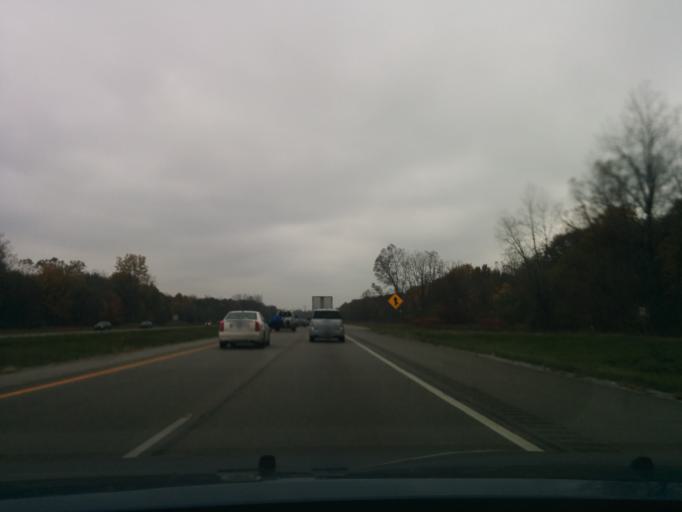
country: US
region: Michigan
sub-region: Wayne County
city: Plymouth
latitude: 42.3612
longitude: -83.5707
